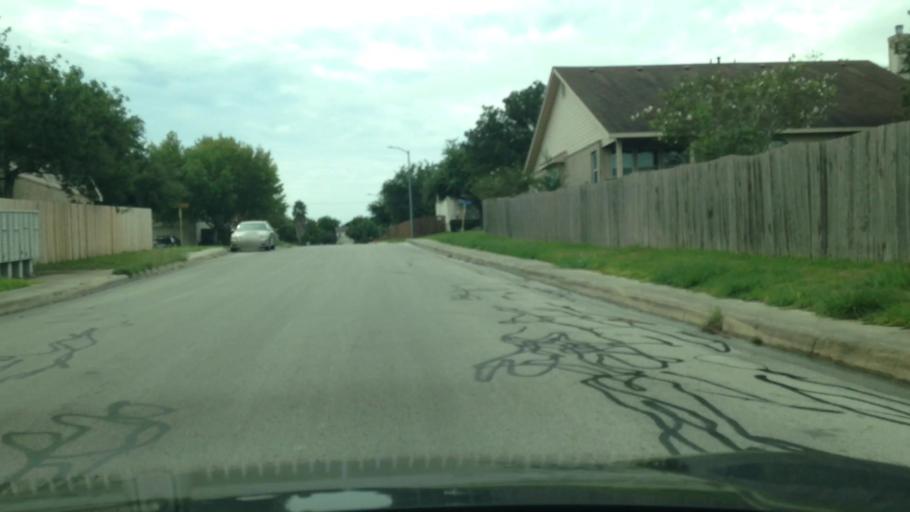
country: US
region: Texas
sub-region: Bexar County
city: Live Oak
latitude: 29.5868
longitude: -98.3842
